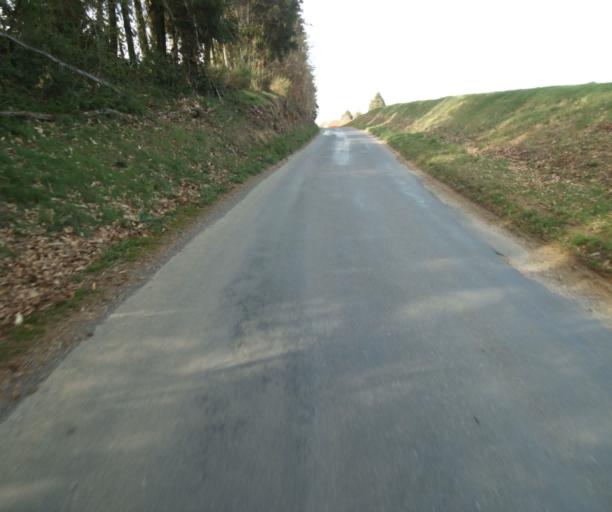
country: FR
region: Limousin
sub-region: Departement de la Correze
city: Naves
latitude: 45.2916
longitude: 1.7407
